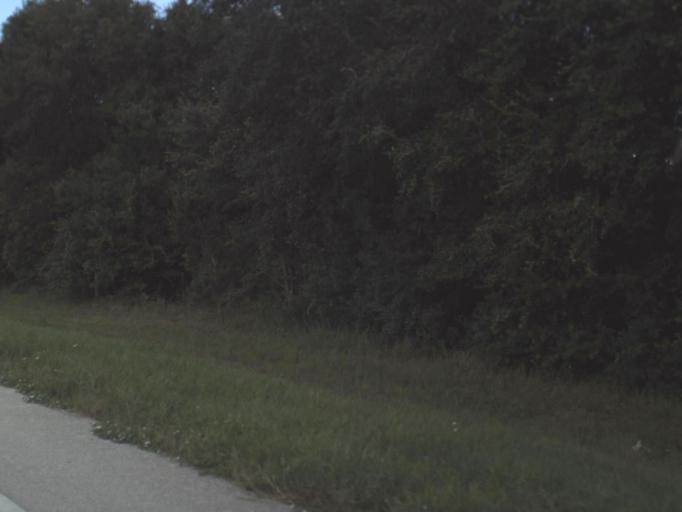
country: US
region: Florida
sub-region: DeSoto County
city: Southeast Arcadia
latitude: 27.2088
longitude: -81.7810
